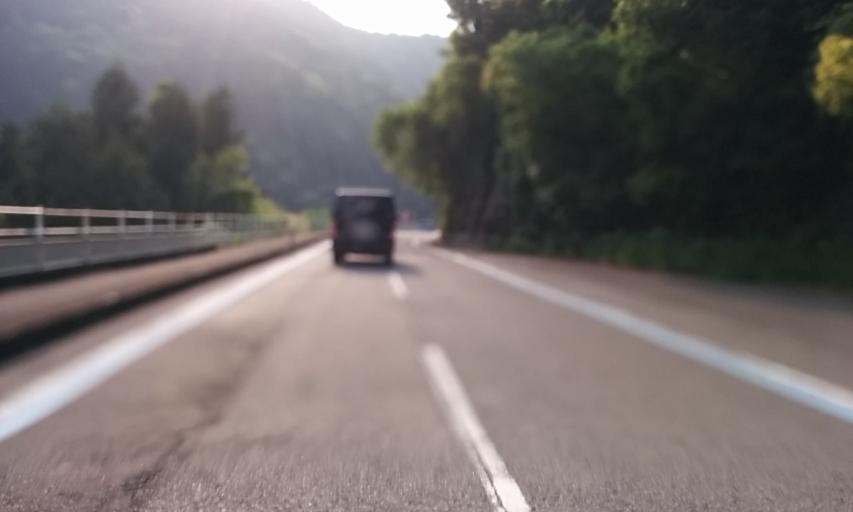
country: JP
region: Ehime
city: Saijo
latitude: 33.8673
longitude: 133.1819
